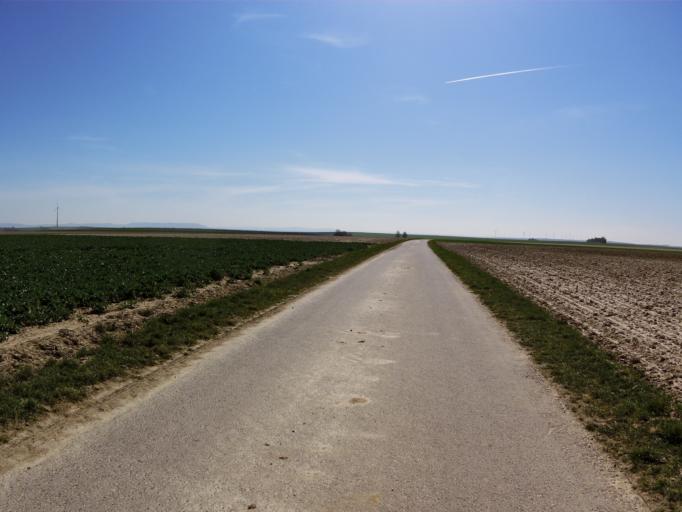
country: DE
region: Bavaria
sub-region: Regierungsbezirk Unterfranken
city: Prosselsheim
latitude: 49.8501
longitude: 10.1232
